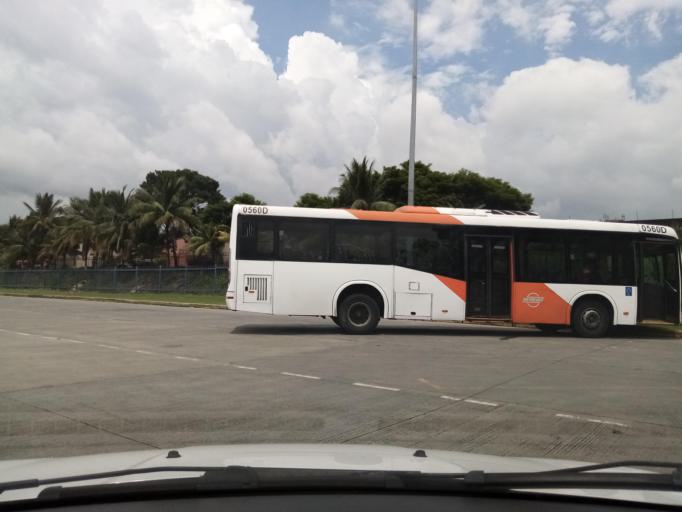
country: PA
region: Panama
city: San Miguelito
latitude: 9.0513
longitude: -79.5054
